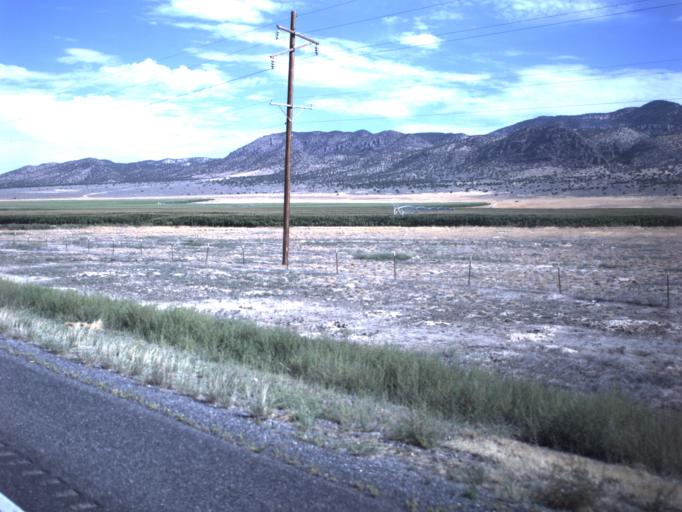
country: US
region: Utah
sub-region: Sanpete County
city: Gunnison
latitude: 39.2516
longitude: -111.8585
